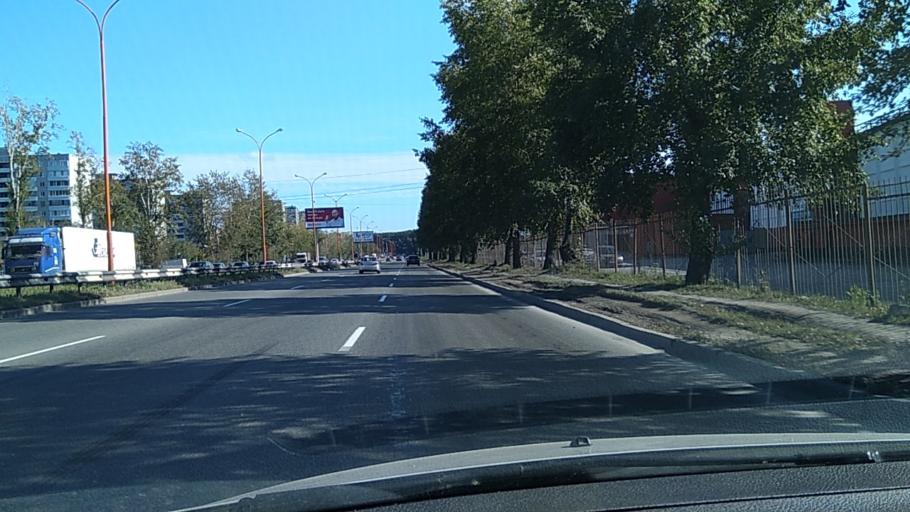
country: RU
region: Sverdlovsk
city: Sovkhoznyy
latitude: 56.7941
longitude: 60.5663
